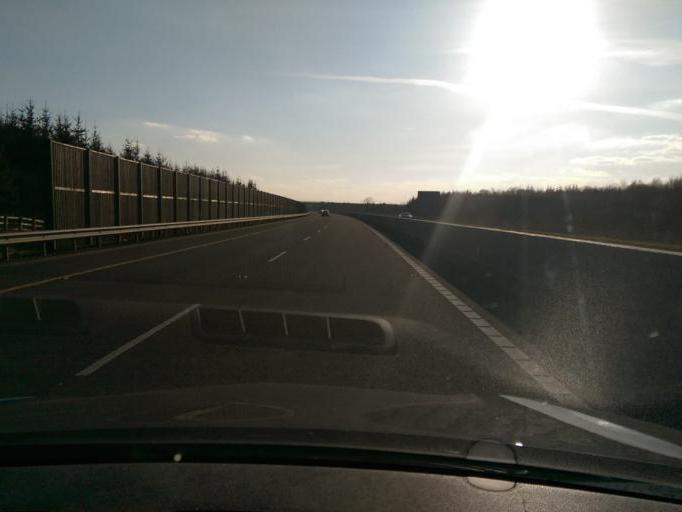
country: IE
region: Leinster
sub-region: Laois
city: Portlaoise
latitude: 53.0113
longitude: -7.3734
